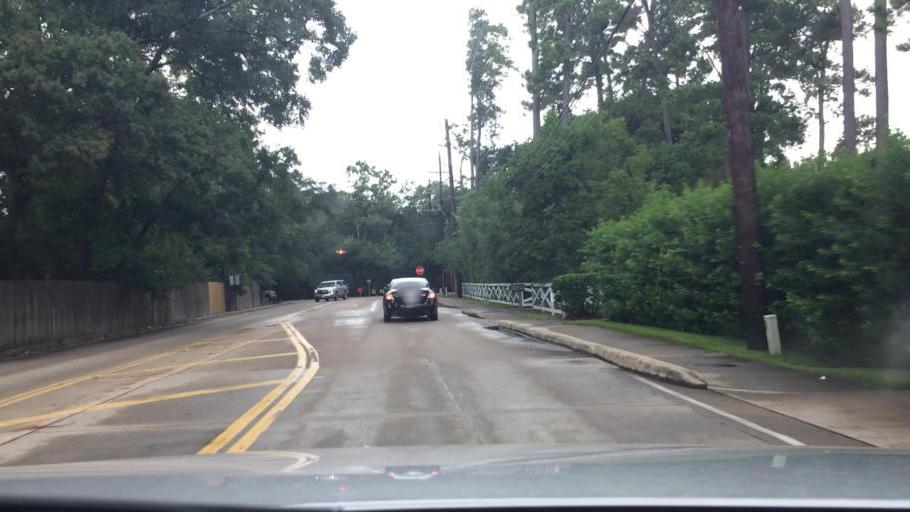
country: US
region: Texas
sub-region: Harris County
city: Hedwig Village
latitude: 29.7742
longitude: -95.5212
